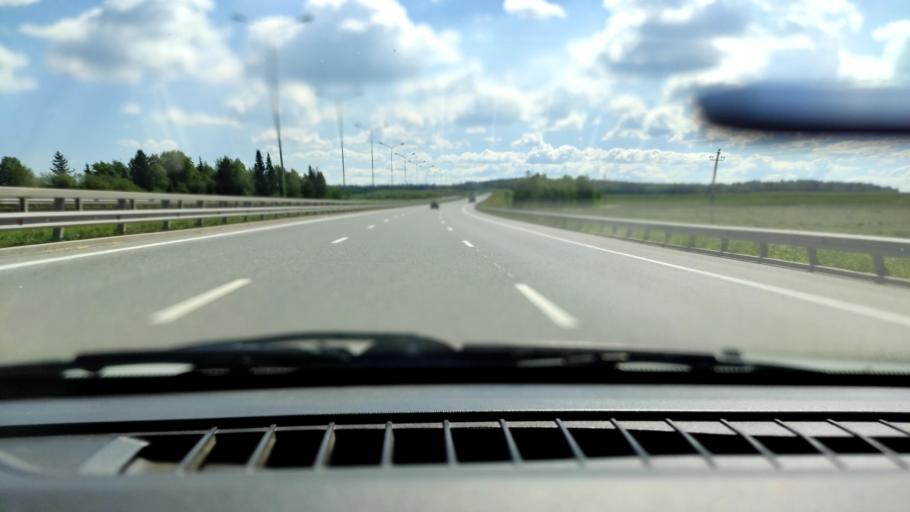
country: RU
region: Perm
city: Zvezdnyy
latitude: 57.7791
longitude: 56.3409
